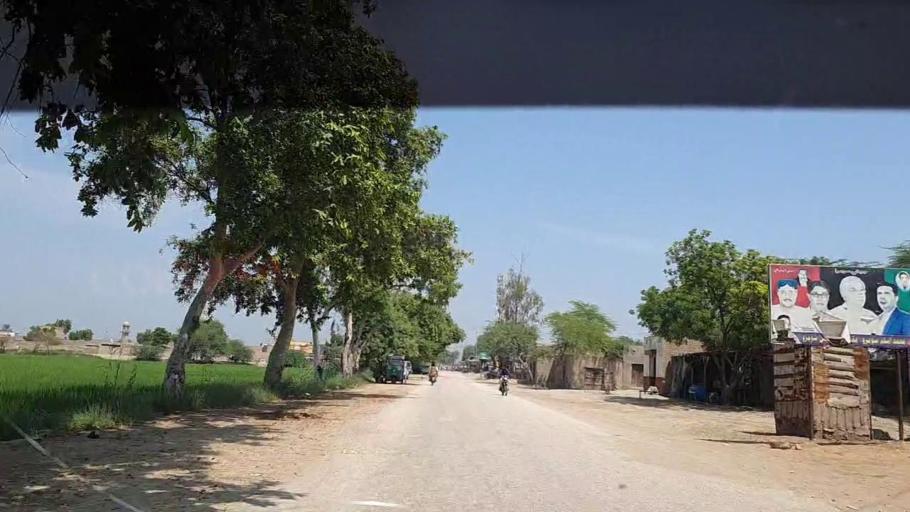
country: PK
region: Sindh
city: Rustam jo Goth
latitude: 28.0772
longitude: 68.7843
